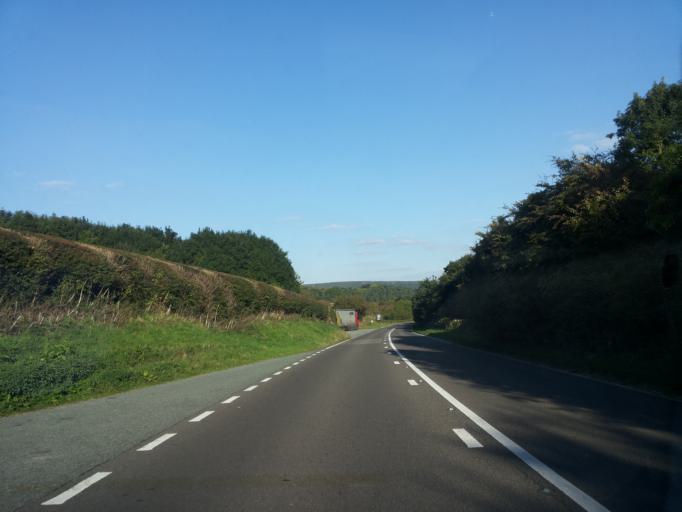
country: GB
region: England
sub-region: Derbyshire
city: Bakewell
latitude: 53.2379
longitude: -1.6535
